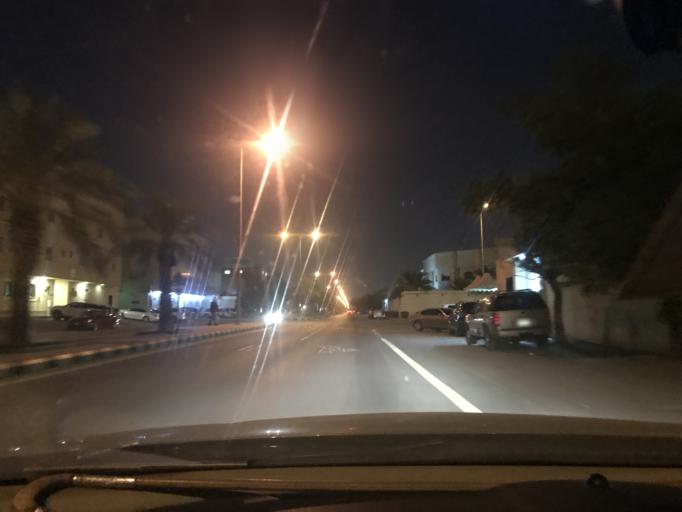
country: SA
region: Ar Riyad
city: Riyadh
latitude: 24.7588
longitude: 46.7461
